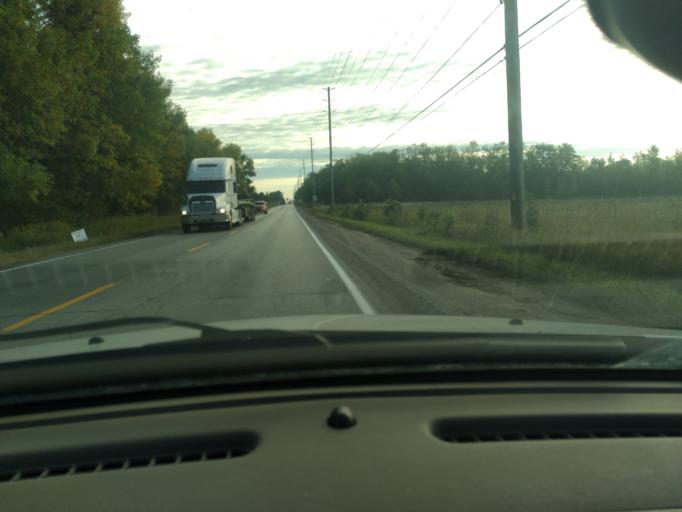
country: CA
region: Ontario
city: Innisfil
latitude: 44.3045
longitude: -79.5937
